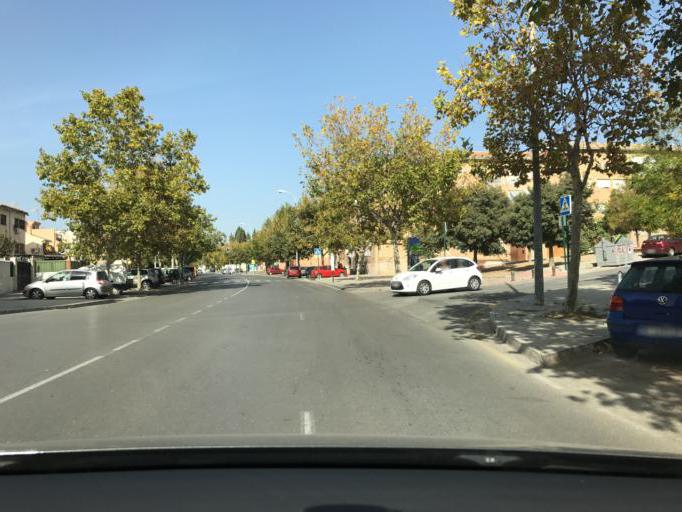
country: ES
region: Andalusia
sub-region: Provincia de Granada
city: Granada
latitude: 37.2039
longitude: -3.6040
